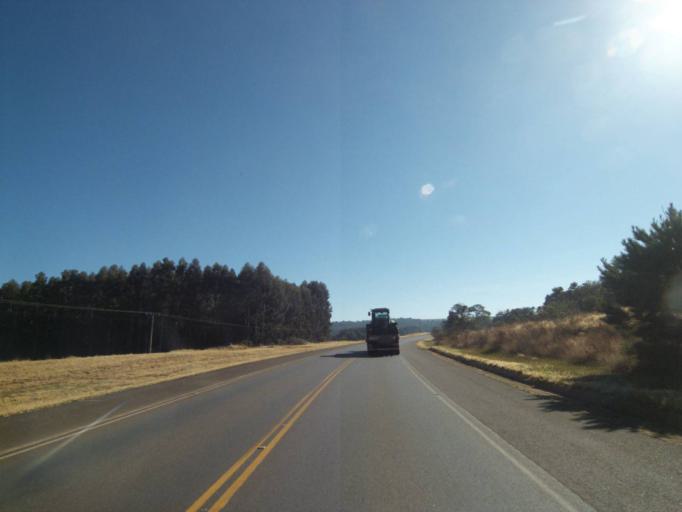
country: BR
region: Parana
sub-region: Tibagi
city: Tibagi
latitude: -24.4764
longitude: -50.4457
